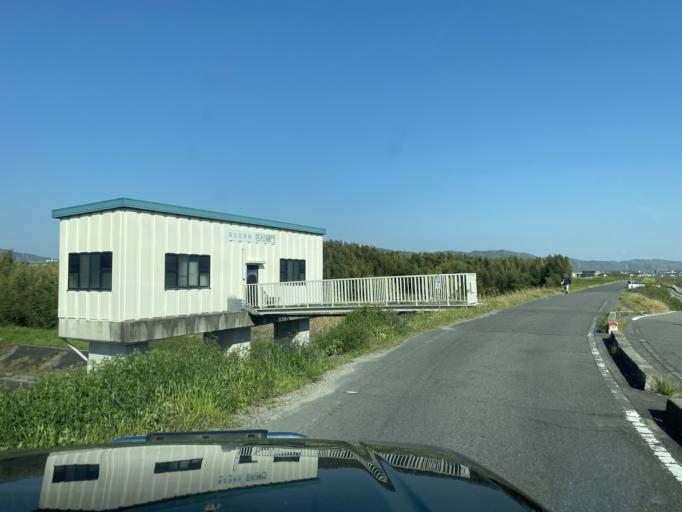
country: JP
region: Kyoto
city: Tanabe
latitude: 34.8331
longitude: 135.7613
